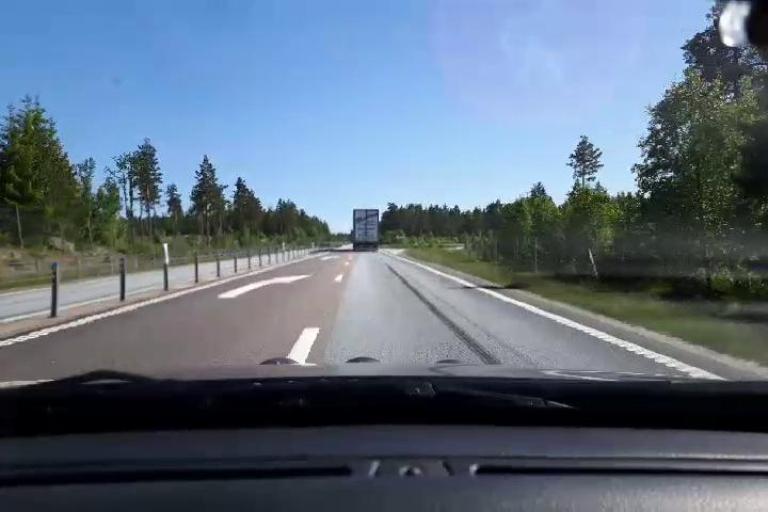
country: SE
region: Gaevleborg
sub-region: Soderhamns Kommun
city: Soderhamn
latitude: 61.2653
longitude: 17.0302
